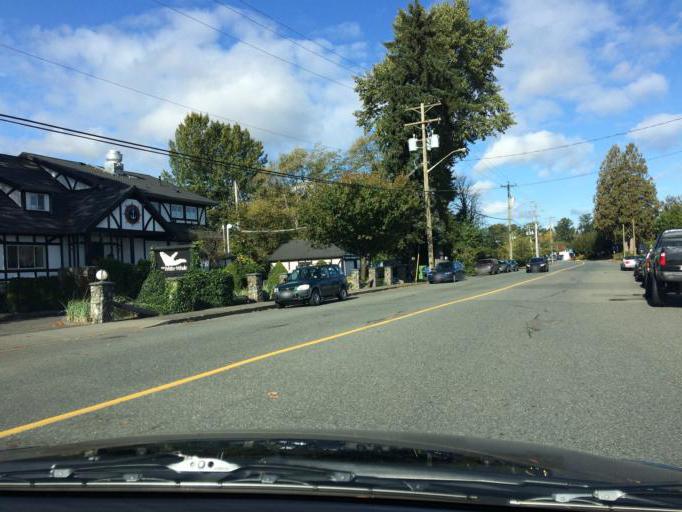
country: CA
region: British Columbia
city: Courtenay
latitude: 49.6911
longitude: -124.9906
